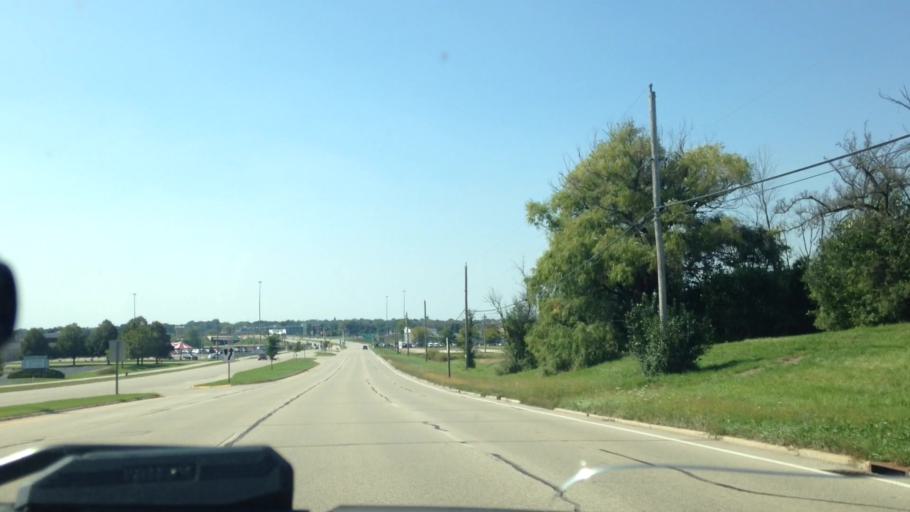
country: US
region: Wisconsin
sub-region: Waukesha County
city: Menomonee Falls
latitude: 43.1777
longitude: -88.0810
